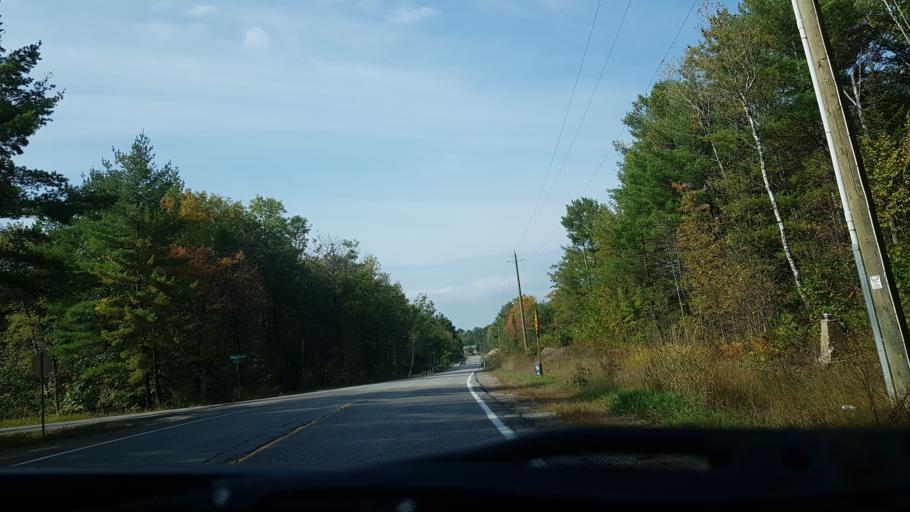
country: CA
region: Ontario
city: Gravenhurst
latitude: 44.7664
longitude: -79.3229
